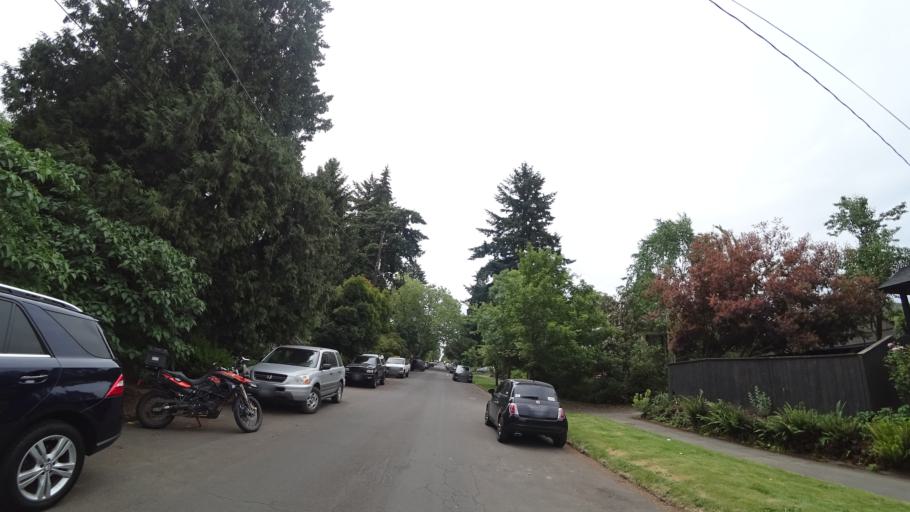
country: US
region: Oregon
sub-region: Multnomah County
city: Portland
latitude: 45.5661
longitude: -122.6339
